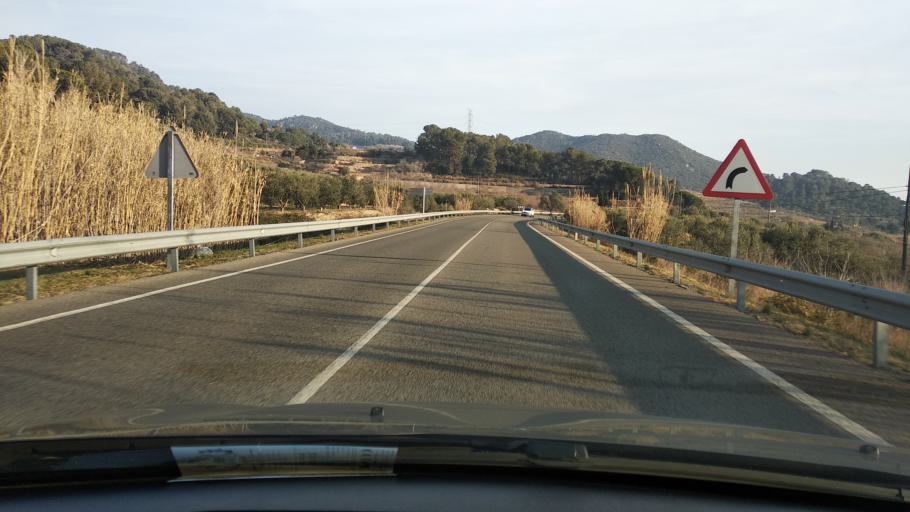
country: ES
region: Catalonia
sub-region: Provincia de Tarragona
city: Alforja
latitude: 41.2038
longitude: 0.9943
